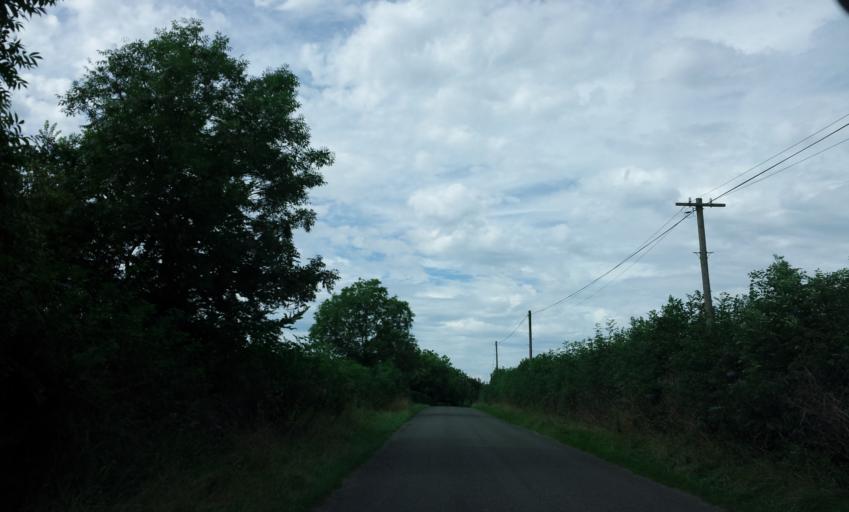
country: IE
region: Leinster
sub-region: Kildare
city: Moone
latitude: 52.9854
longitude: -6.8415
